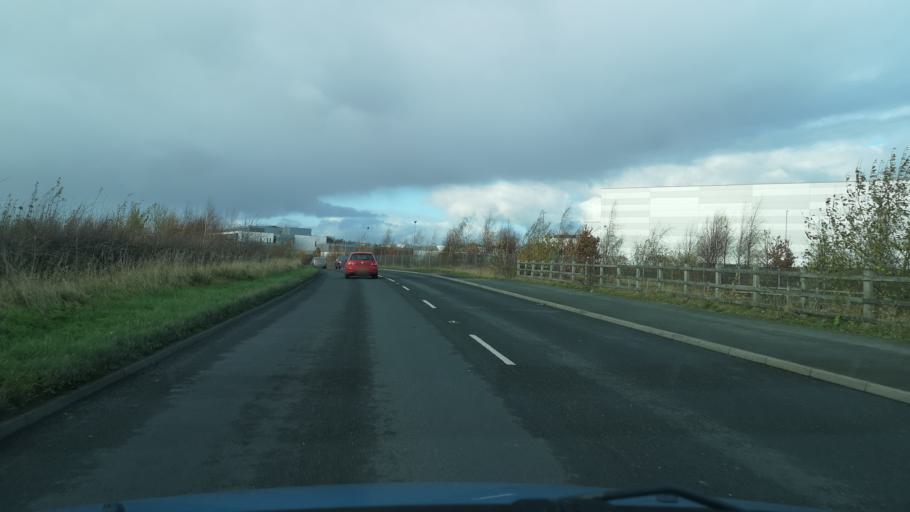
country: GB
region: England
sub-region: City and Borough of Wakefield
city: Normanton
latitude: 53.6966
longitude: -1.3843
